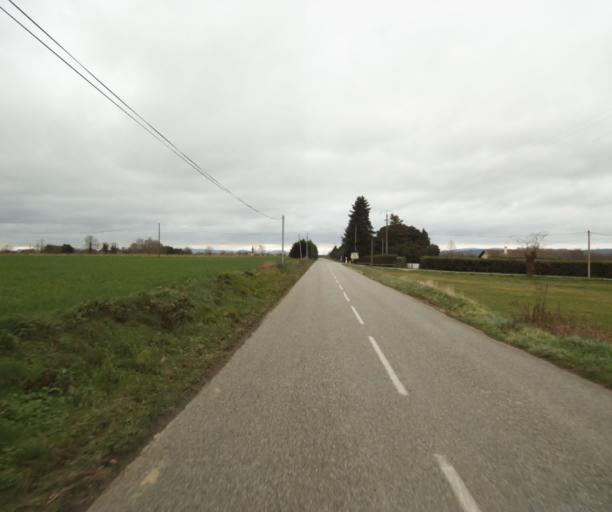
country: FR
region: Midi-Pyrenees
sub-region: Departement de l'Ariege
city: Pamiers
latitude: 43.1658
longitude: 1.6362
